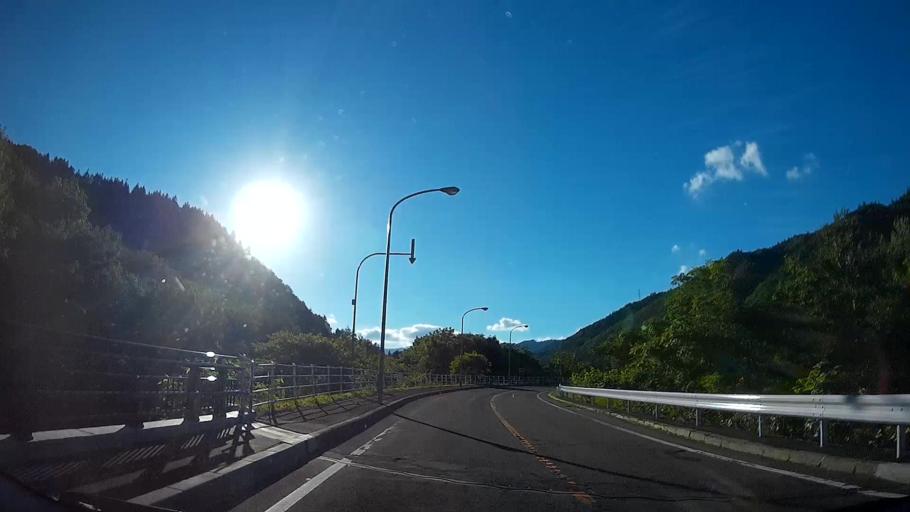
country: JP
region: Hokkaido
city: Sapporo
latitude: 42.9773
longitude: 141.1363
